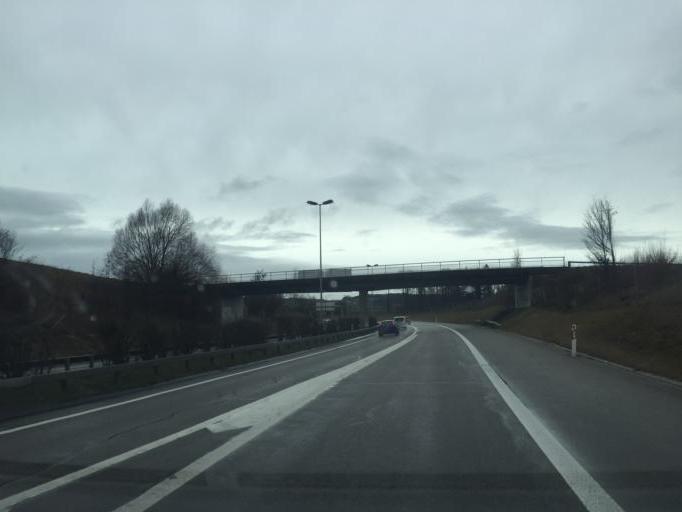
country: CH
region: Zurich
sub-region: Bezirk Winterthur
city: Wuelflingen (Kreis 6) / Lindenplatz
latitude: 47.5254
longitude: 8.7013
